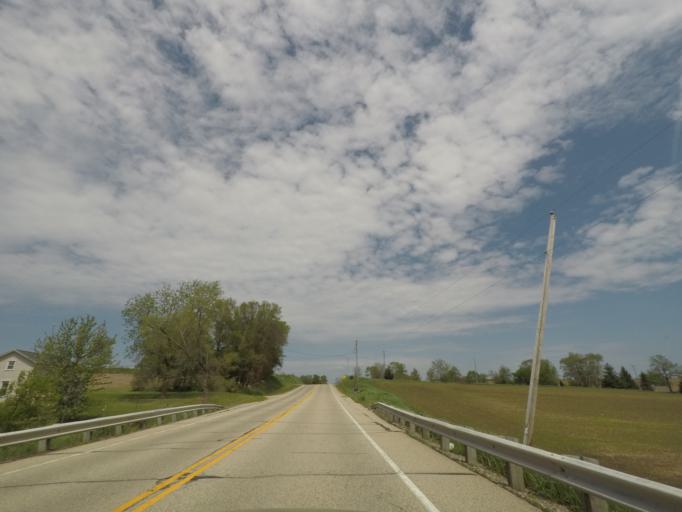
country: US
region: Wisconsin
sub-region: Rock County
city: Orfordville
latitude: 42.7000
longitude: -89.2885
